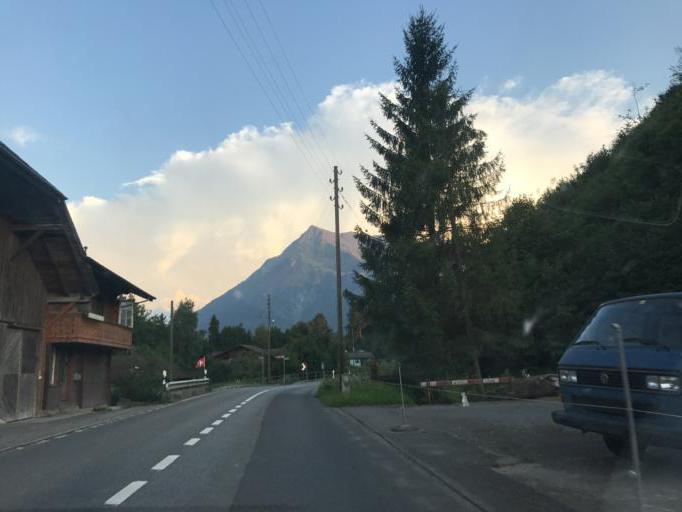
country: CH
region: Bern
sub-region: Frutigen-Niedersimmental District
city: Wimmis
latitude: 46.7065
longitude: 7.6311
